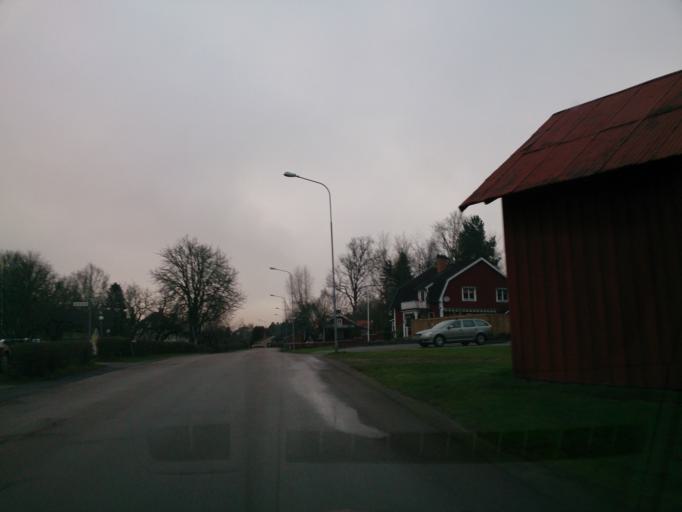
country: SE
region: OEstergoetland
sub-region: Atvidabergs Kommun
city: Atvidaberg
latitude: 58.3332
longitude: 16.0227
